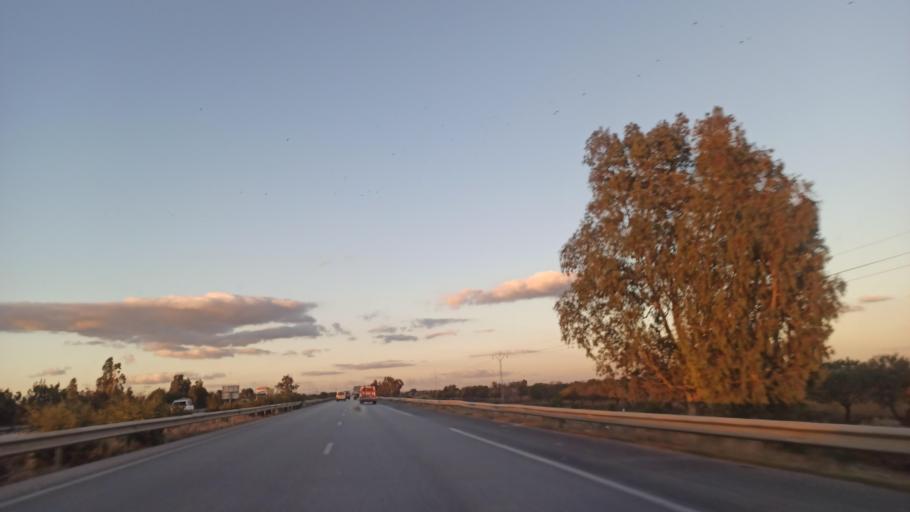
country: TN
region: Susah
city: Harqalah
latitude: 36.1262
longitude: 10.4063
